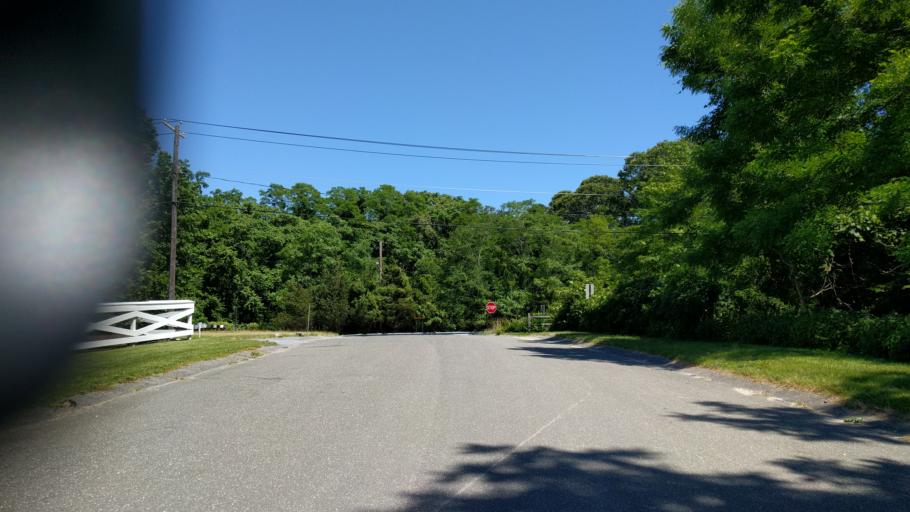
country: US
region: New York
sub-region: Suffolk County
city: Noyack
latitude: 40.9849
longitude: -72.3741
